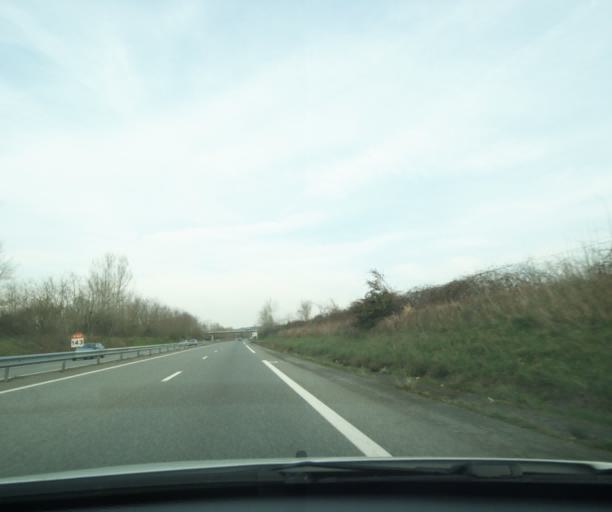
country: FR
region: Midi-Pyrenees
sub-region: Departement des Hautes-Pyrenees
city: Laloubere
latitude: 43.2140
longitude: 0.0825
